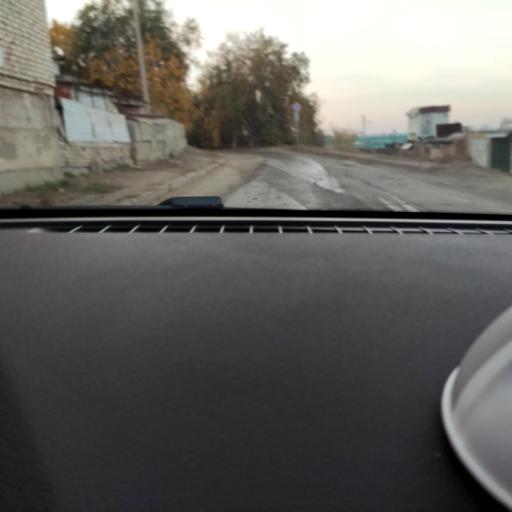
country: RU
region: Samara
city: Samara
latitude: 53.1835
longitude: 50.1437
